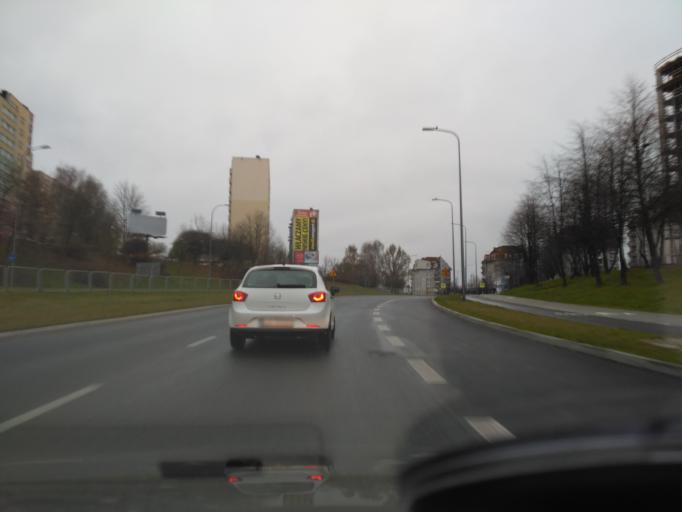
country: PL
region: Lublin Voivodeship
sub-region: Powiat lubelski
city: Lublin
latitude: 51.2547
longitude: 22.5525
